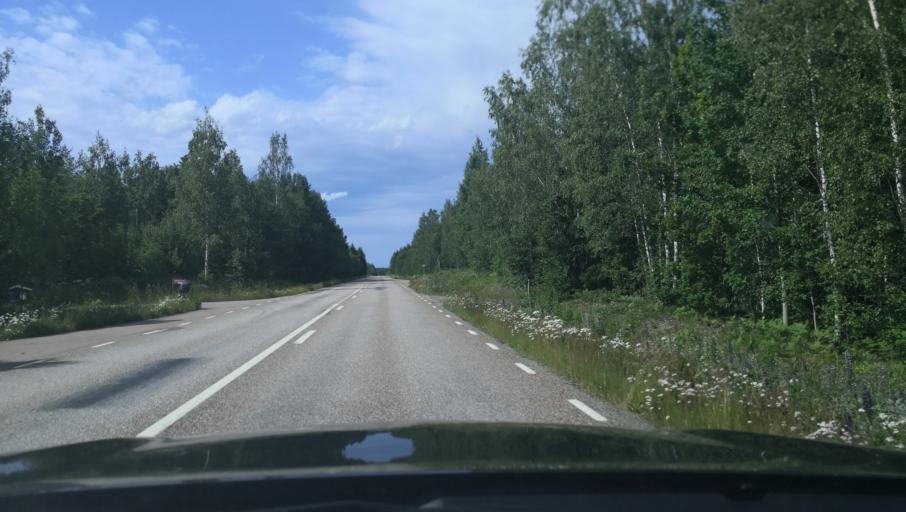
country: SE
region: Vaestmanland
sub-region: Surahammars Kommun
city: Ramnas
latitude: 59.9515
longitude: 16.2237
